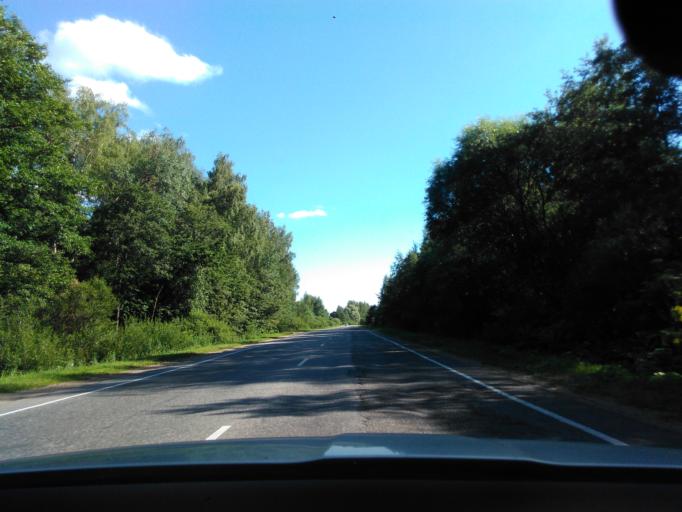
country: RU
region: Tverskaya
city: Konakovo
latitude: 56.6467
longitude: 36.7088
